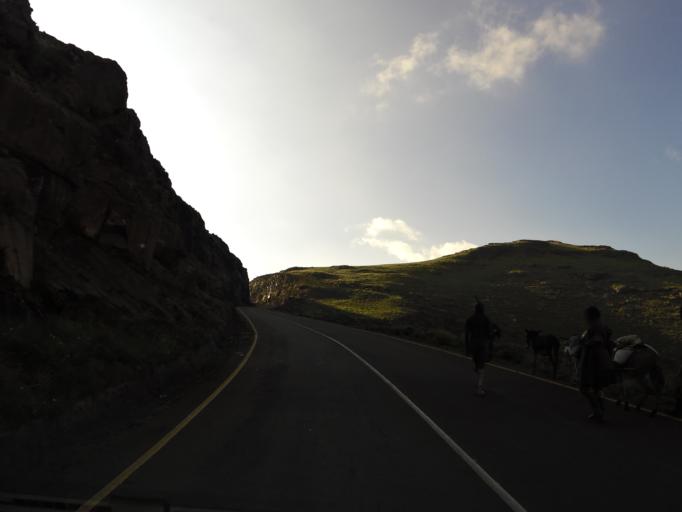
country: LS
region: Butha-Buthe
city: Butha-Buthe
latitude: -29.1047
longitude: 28.4288
